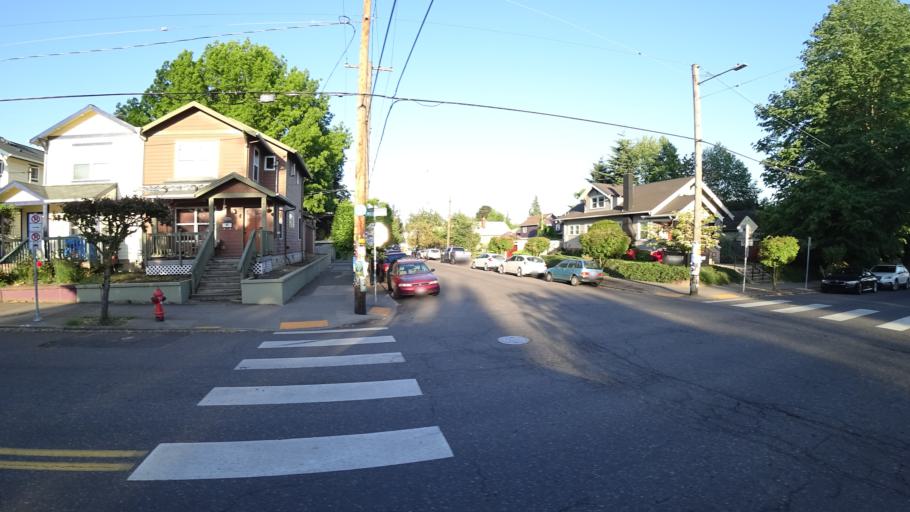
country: US
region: Oregon
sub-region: Multnomah County
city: Portland
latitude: 45.5535
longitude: -122.6756
